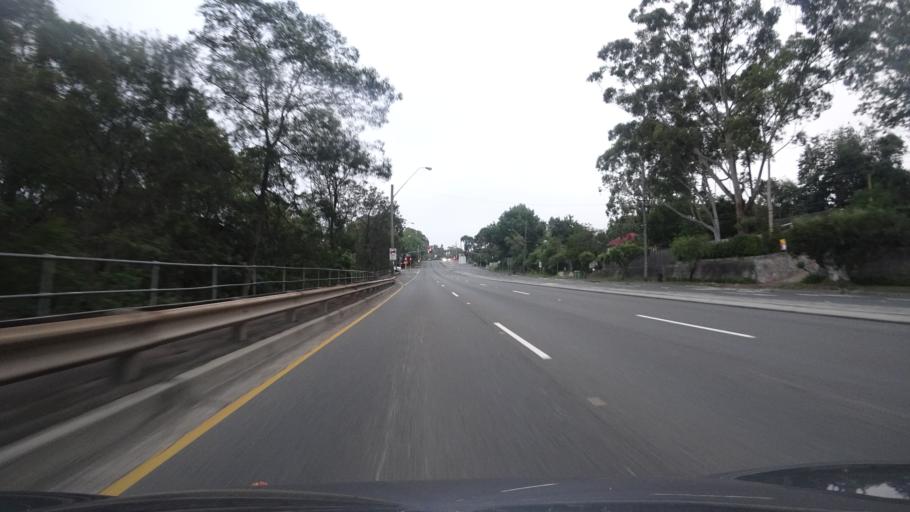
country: AU
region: New South Wales
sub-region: Ryde
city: Macquarie Park
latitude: -33.7704
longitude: 151.1358
